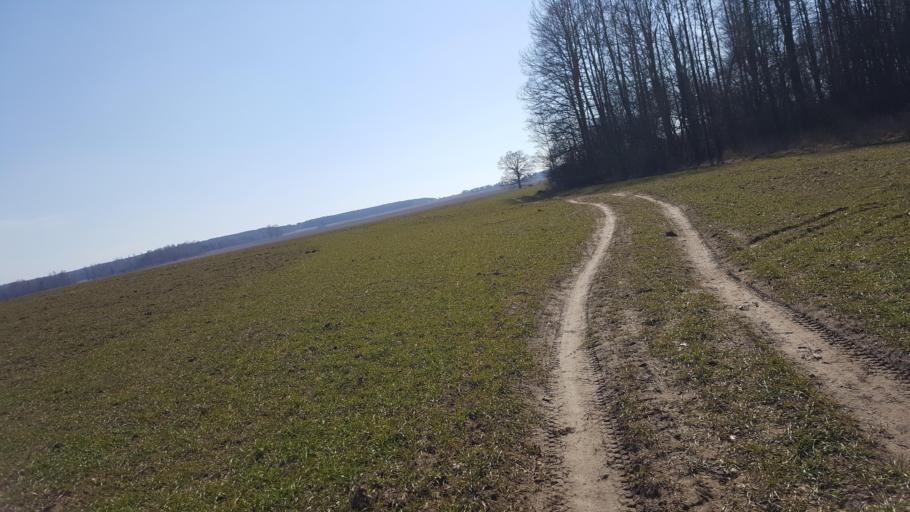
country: BY
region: Brest
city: Kamyanyets
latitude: 52.3654
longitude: 23.7653
